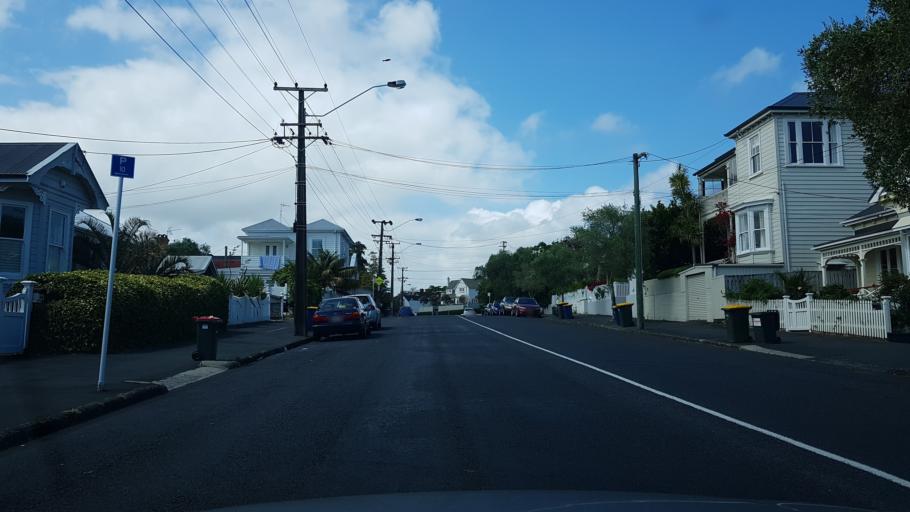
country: NZ
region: Auckland
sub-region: Auckland
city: Auckland
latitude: -36.8265
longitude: 174.8029
